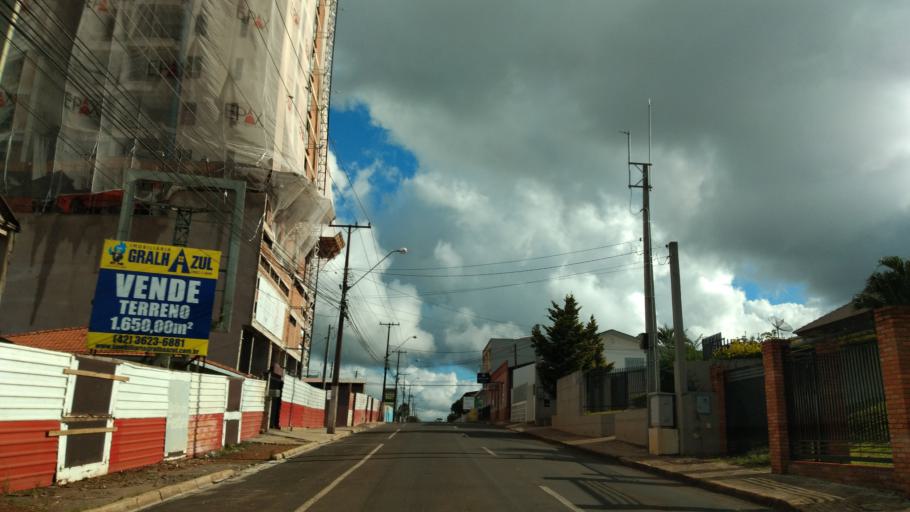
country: BR
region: Parana
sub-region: Guarapuava
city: Guarapuava
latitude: -25.3969
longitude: -51.4730
